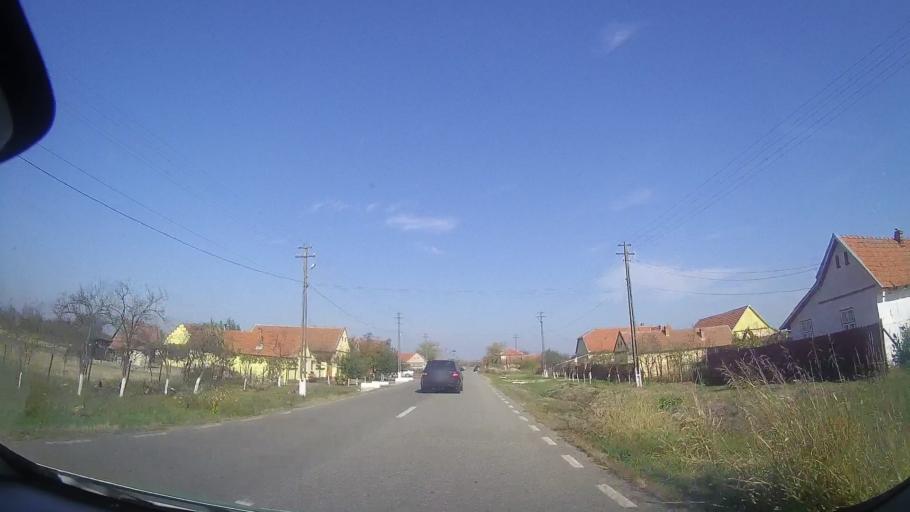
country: RO
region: Timis
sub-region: Comuna Ghizela
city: Ghizela
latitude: 45.7919
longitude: 21.7294
